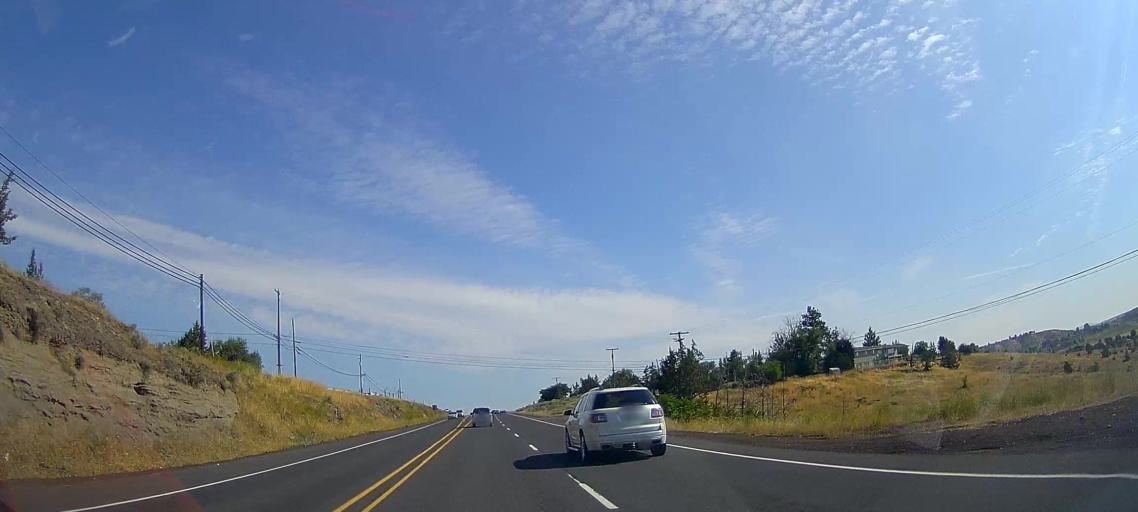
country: US
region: Oregon
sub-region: Jefferson County
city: Madras
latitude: 44.6496
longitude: -121.1290
